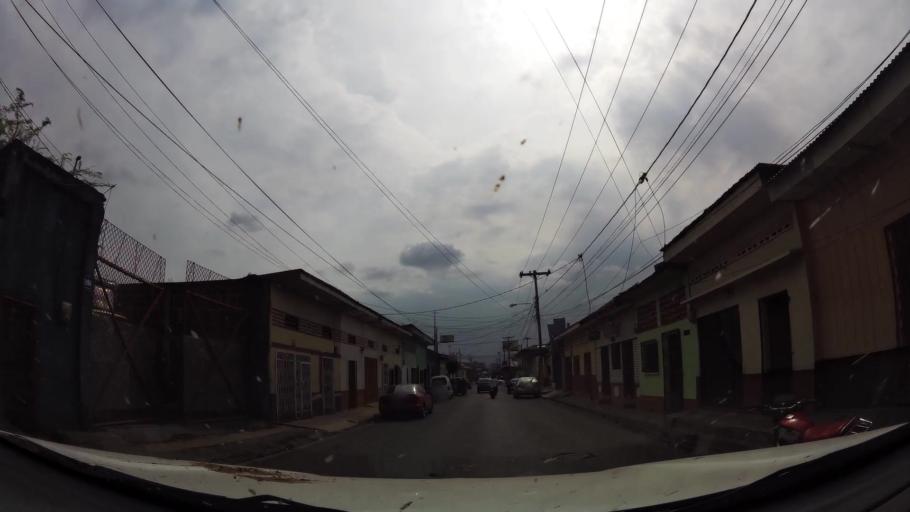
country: NI
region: Masaya
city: Masaya
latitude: 11.9753
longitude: -86.0910
